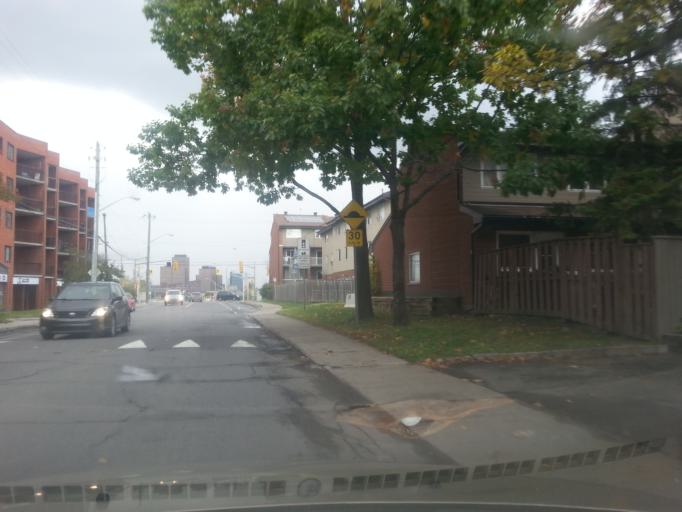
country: CA
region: Ontario
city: Ottawa
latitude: 45.4121
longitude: -75.7121
